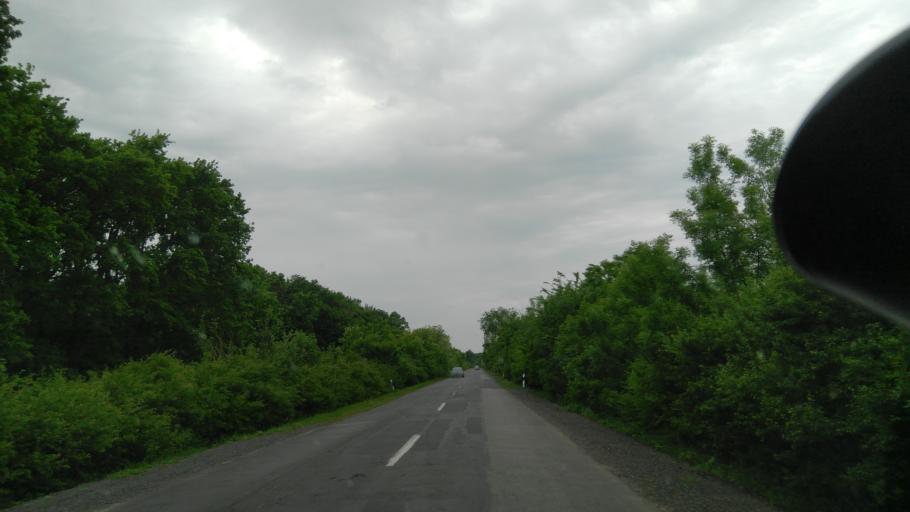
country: HU
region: Bekes
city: Doboz
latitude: 46.7215
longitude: 21.3110
